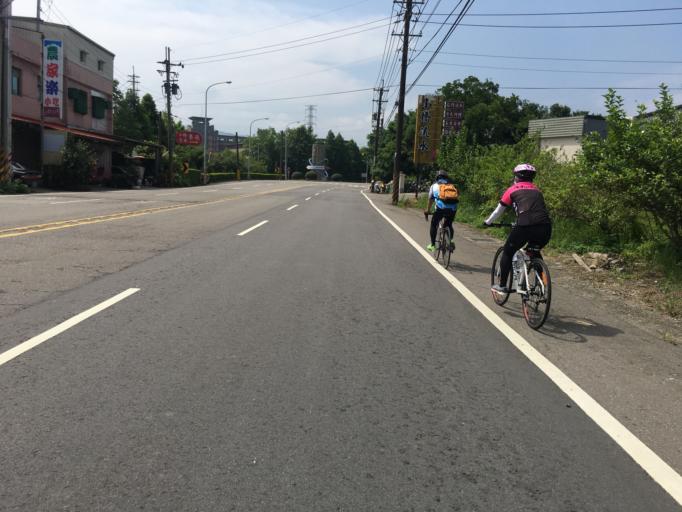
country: TW
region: Taiwan
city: Daxi
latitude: 24.8589
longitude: 121.2508
